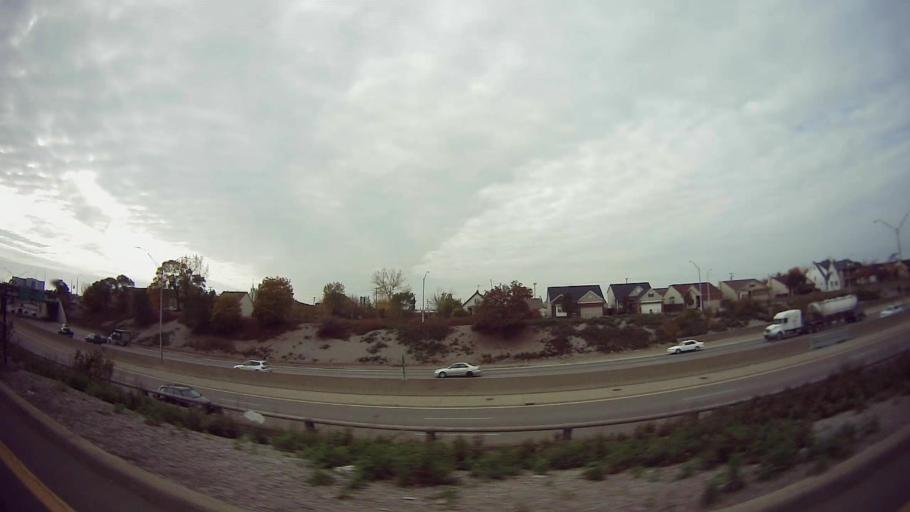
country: US
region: Michigan
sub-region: Wayne County
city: Hamtramck
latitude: 42.3981
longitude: -83.0687
